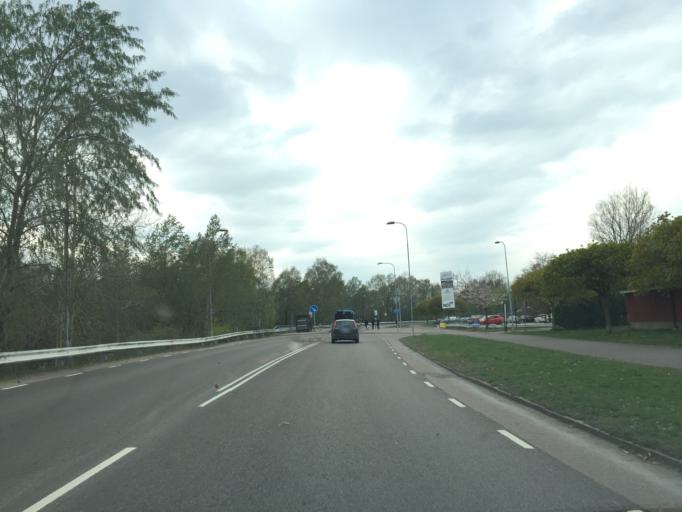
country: SE
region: Vaestra Goetaland
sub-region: Goteborg
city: Loevgaerdet
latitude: 57.8160
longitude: 12.0347
